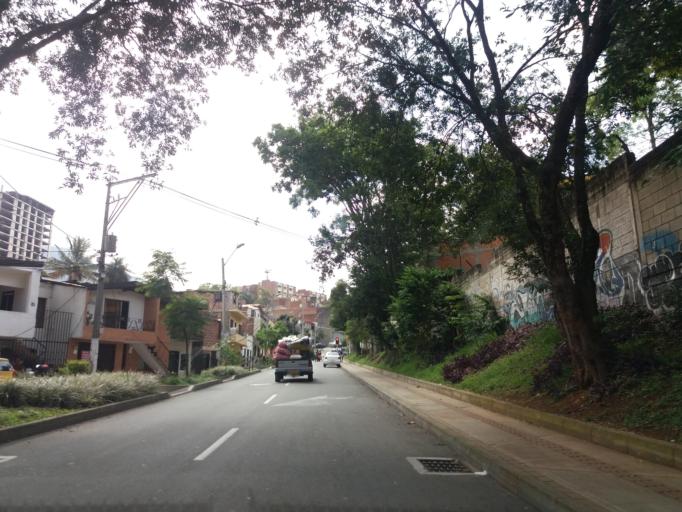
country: CO
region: Antioquia
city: Medellin
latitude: 6.2844
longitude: -75.5623
